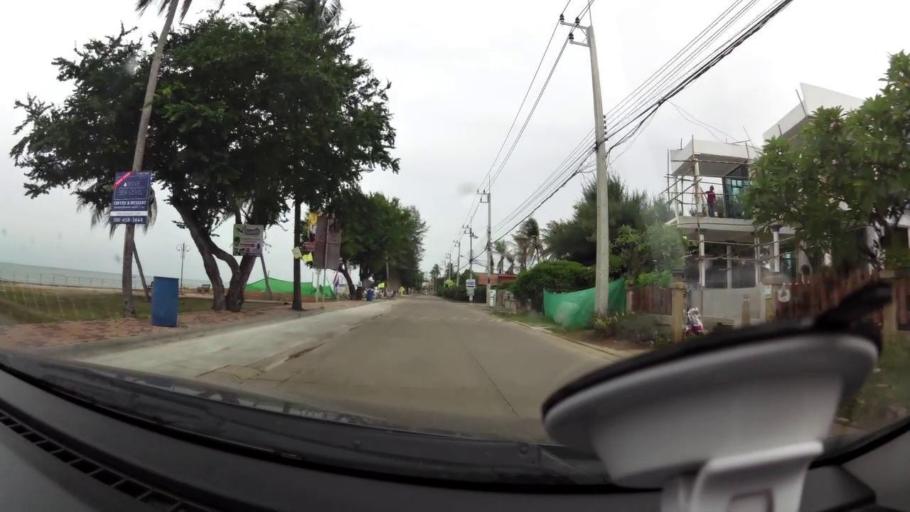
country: TH
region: Prachuap Khiri Khan
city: Pran Buri
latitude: 12.3977
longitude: 99.9948
